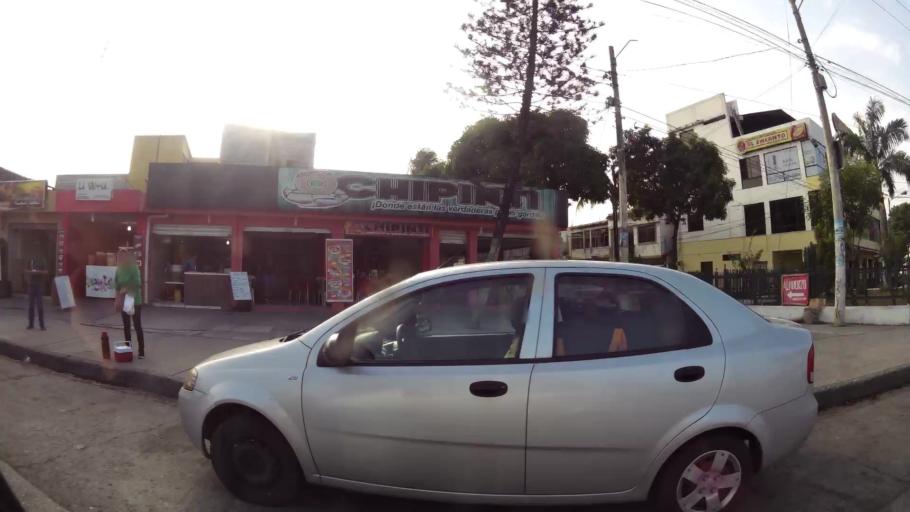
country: EC
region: Guayas
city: Eloy Alfaro
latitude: -2.1272
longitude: -79.9006
